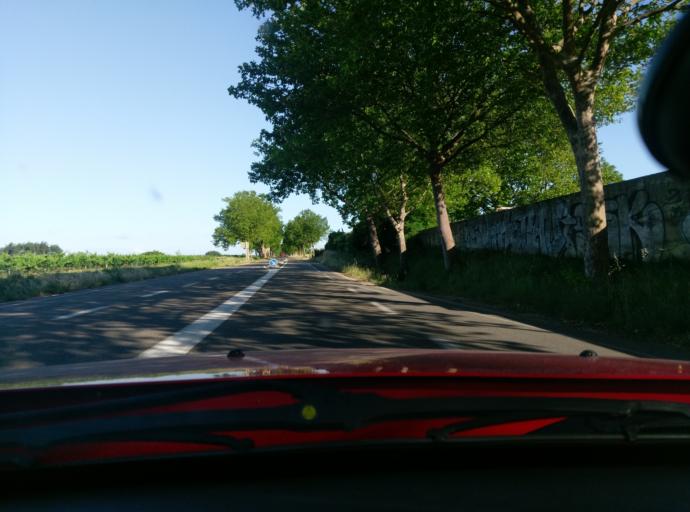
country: FR
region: Languedoc-Roussillon
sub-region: Departement du Gard
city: Castillon-du-Gard
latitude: 43.9667
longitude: 4.5089
